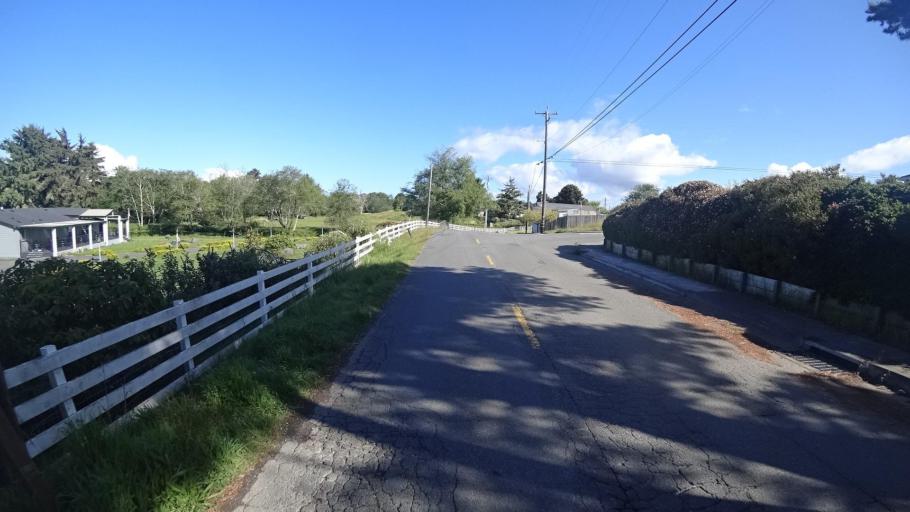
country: US
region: California
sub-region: Humboldt County
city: McKinleyville
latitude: 40.9605
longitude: -124.1139
